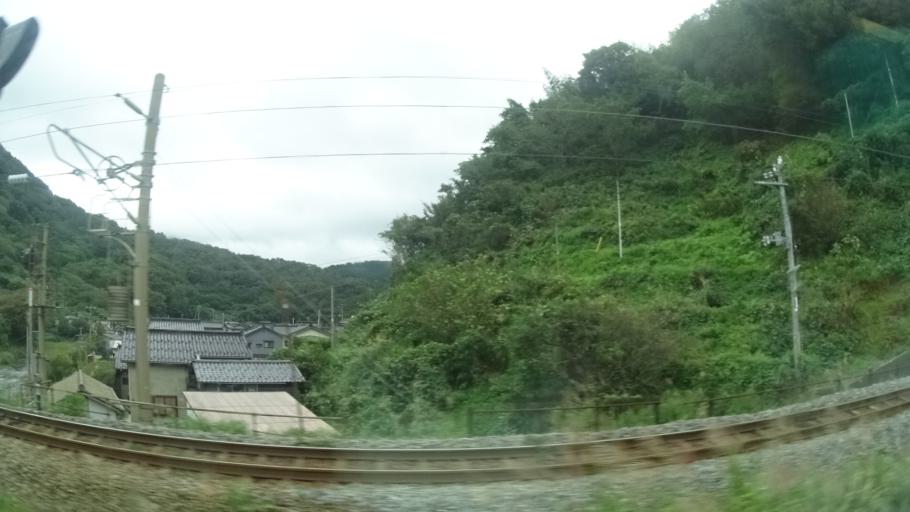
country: JP
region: Yamagata
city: Tsuruoka
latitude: 38.6717
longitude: 139.6188
